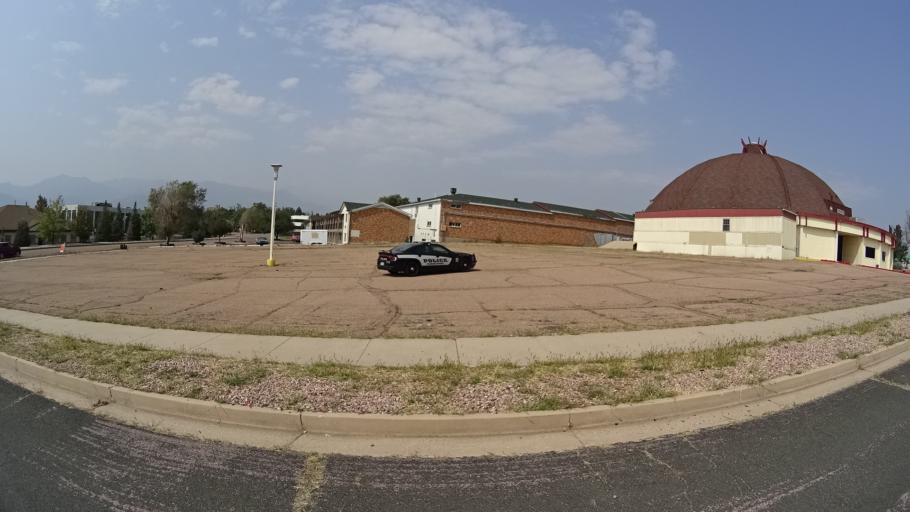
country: US
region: Colorado
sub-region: El Paso County
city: Colorado Springs
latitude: 38.8313
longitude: -104.7849
